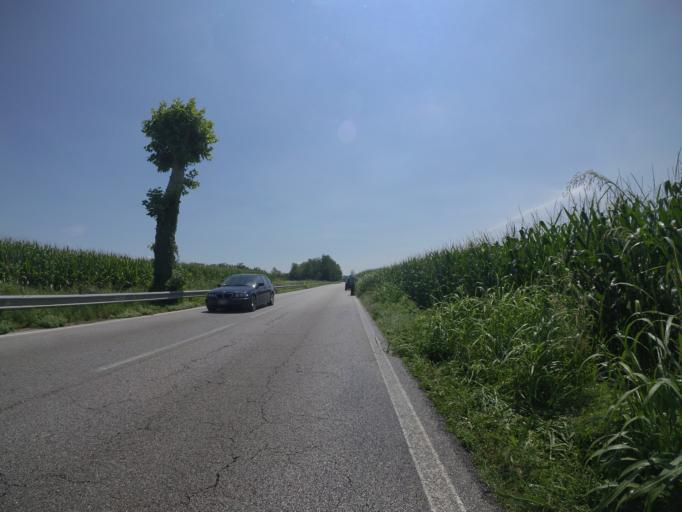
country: IT
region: Friuli Venezia Giulia
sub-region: Provincia di Udine
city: Basiliano-Vissandone
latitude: 46.0002
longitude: 13.1193
